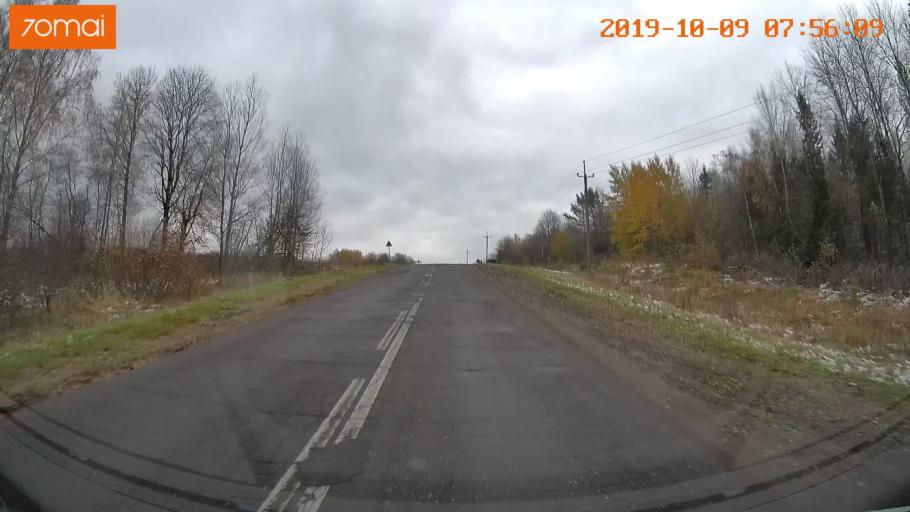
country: RU
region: Jaroslavl
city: Kukoboy
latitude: 58.6986
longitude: 39.9316
